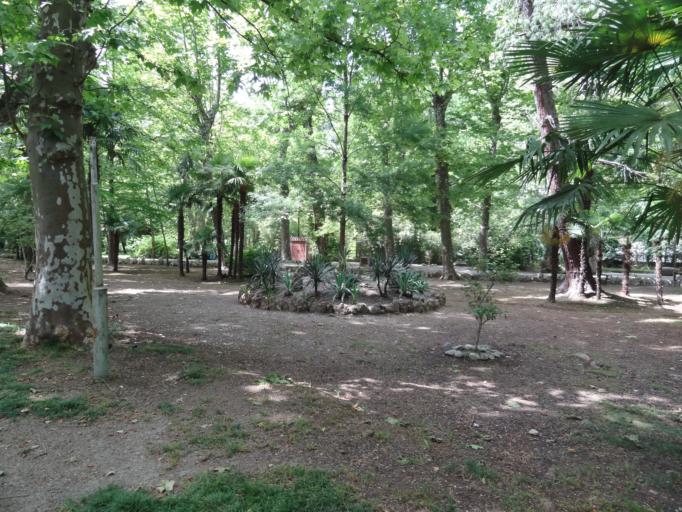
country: GE
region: Abkhazia
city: Gagra
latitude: 43.3242
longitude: 40.2283
